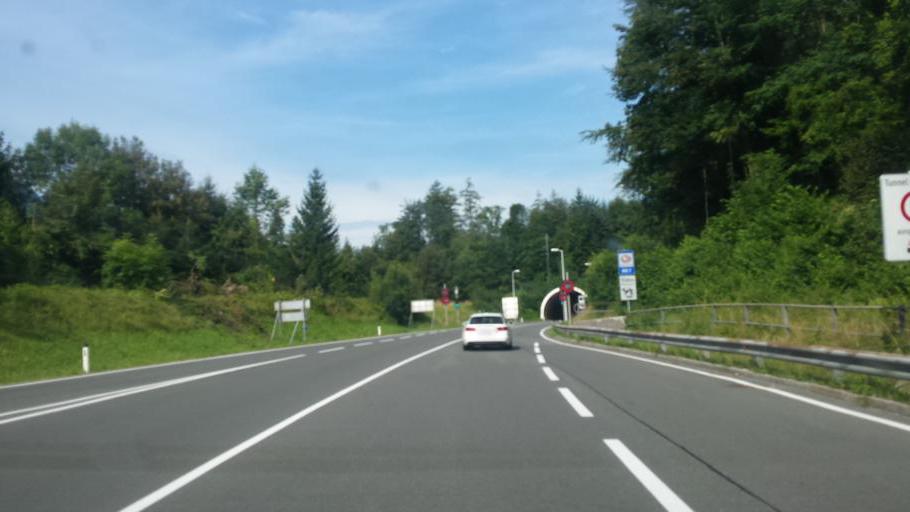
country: AT
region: Upper Austria
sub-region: Politischer Bezirk Gmunden
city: Bad Ischl
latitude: 47.7162
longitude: 13.6249
